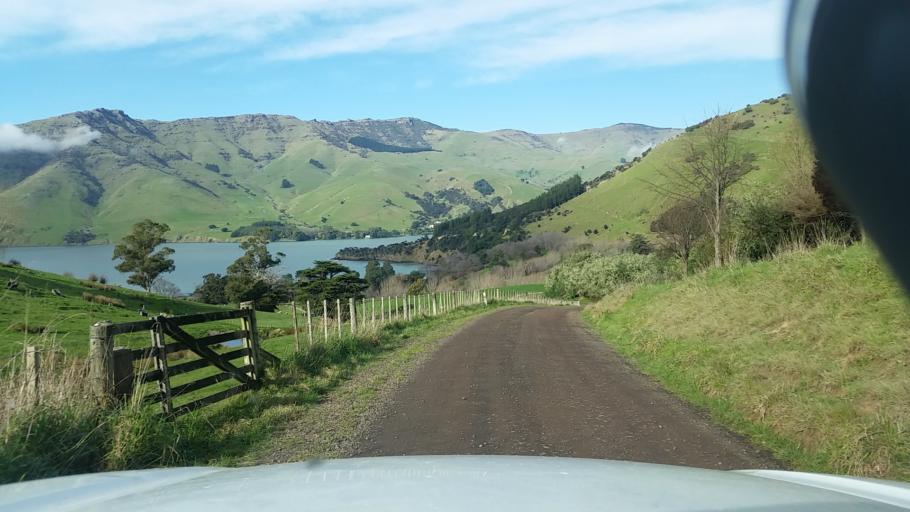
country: NZ
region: Canterbury
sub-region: Christchurch City
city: Christchurch
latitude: -43.6713
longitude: 172.8742
